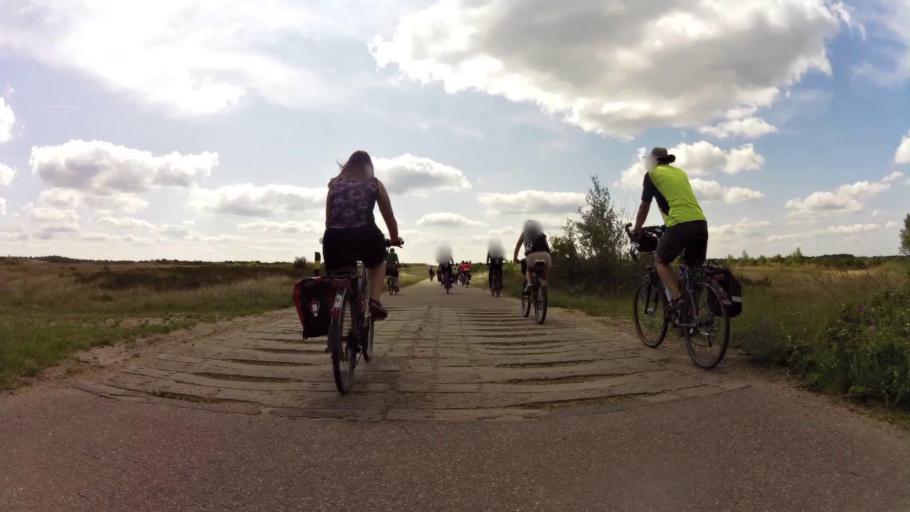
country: PL
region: West Pomeranian Voivodeship
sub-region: Powiat drawski
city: Drawsko Pomorskie
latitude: 53.4232
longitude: 15.7618
